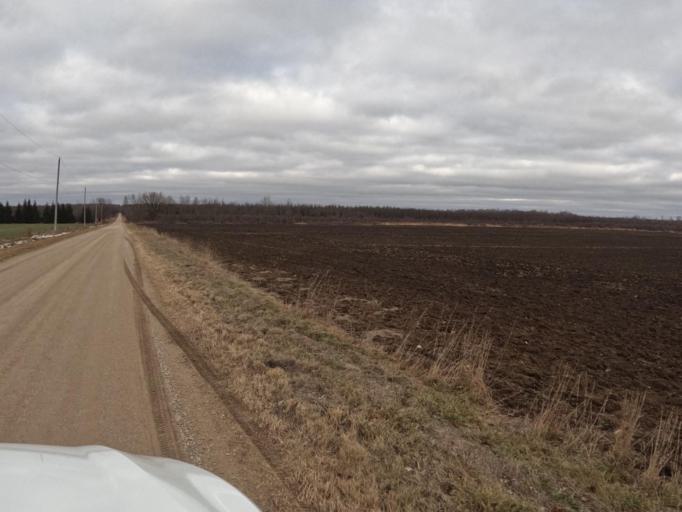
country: CA
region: Ontario
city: Shelburne
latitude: 43.8928
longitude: -80.4070
